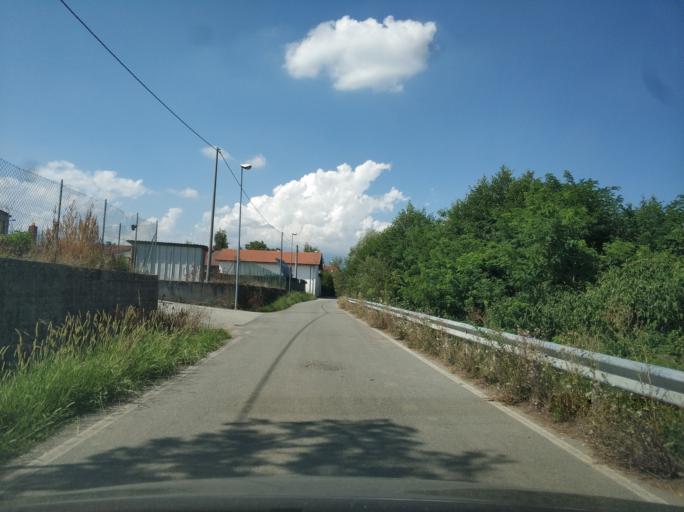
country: IT
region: Piedmont
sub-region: Provincia di Torino
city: Rivarolo Canavese
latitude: 45.3129
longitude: 7.7233
